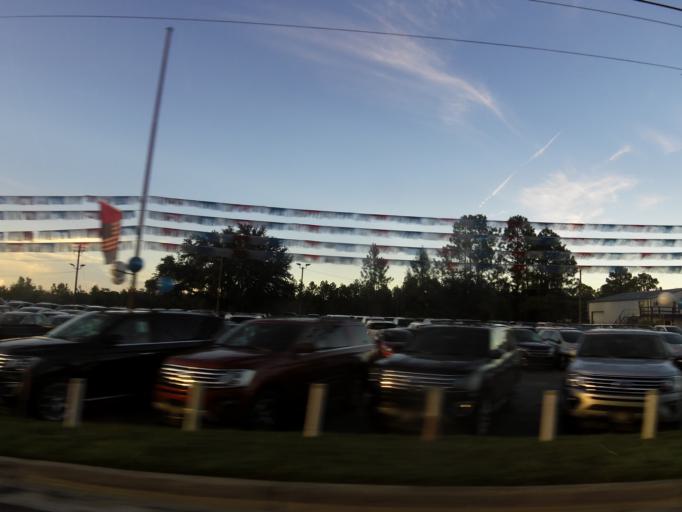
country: US
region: Georgia
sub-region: Camden County
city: St Marys
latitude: 30.7803
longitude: -81.6254
